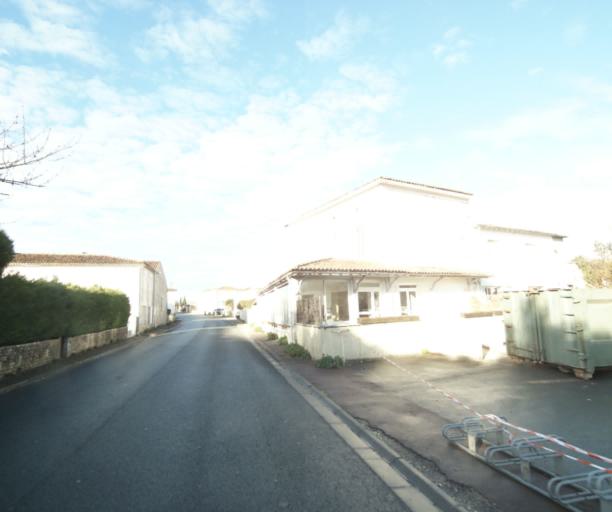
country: FR
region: Poitou-Charentes
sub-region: Departement de la Charente-Maritime
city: Corme-Royal
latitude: 45.7020
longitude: -0.7832
